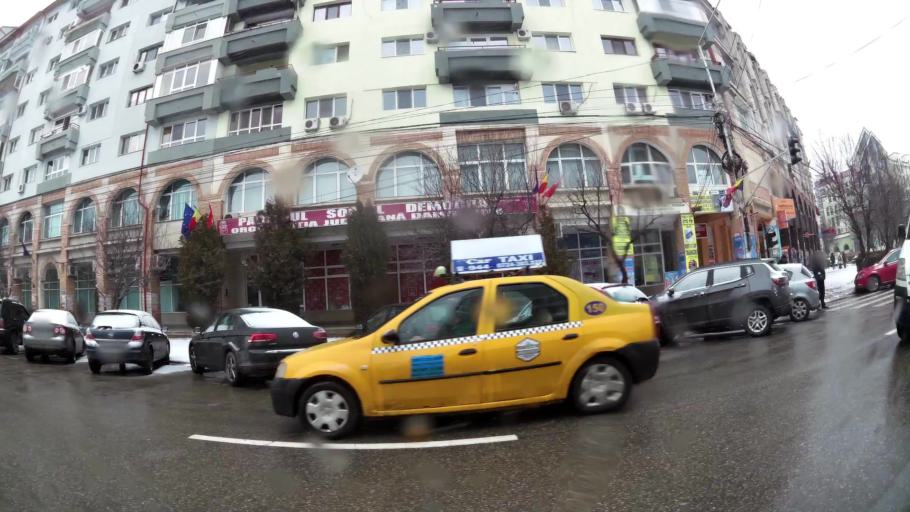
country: RO
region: Dambovita
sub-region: Municipiul Targoviste
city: Targoviste
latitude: 44.9272
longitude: 25.4609
